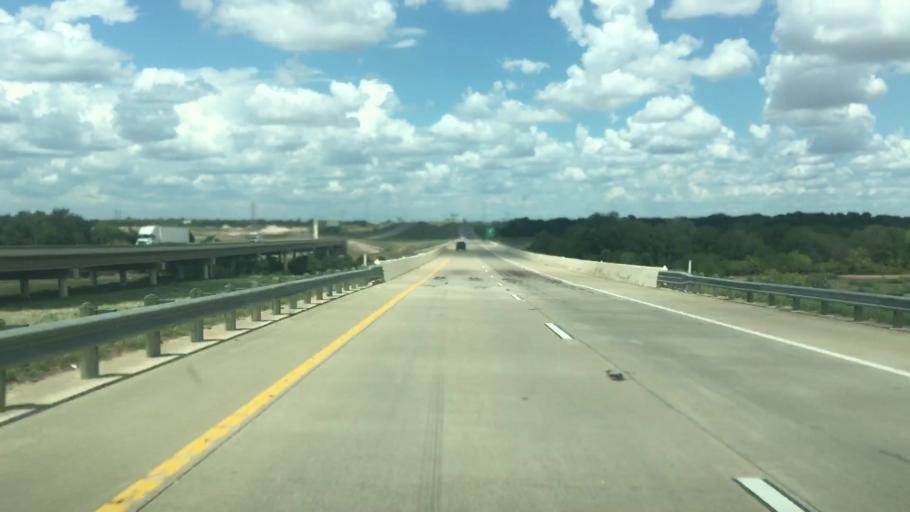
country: US
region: Texas
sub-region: Williamson County
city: Georgetown
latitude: 30.6530
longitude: -97.6355
